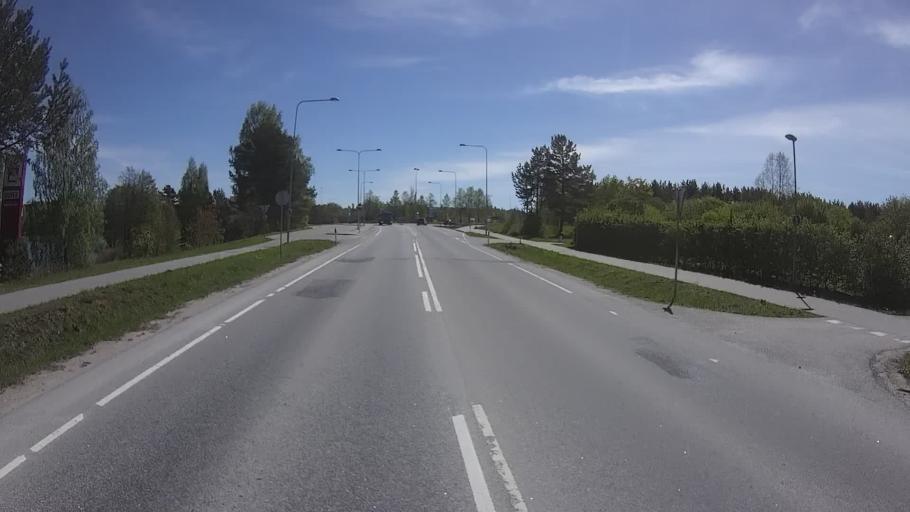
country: EE
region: Vorumaa
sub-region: Voru linn
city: Voru
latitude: 57.8168
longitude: 27.0280
